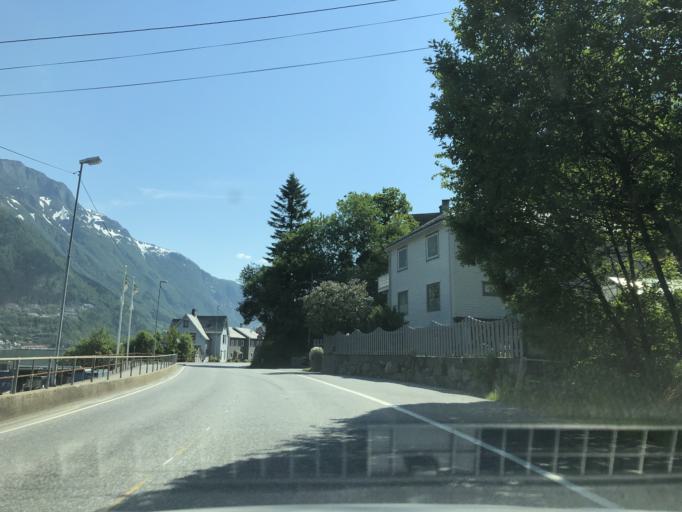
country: NO
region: Hordaland
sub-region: Odda
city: Odda
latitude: 60.0837
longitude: 6.5304
